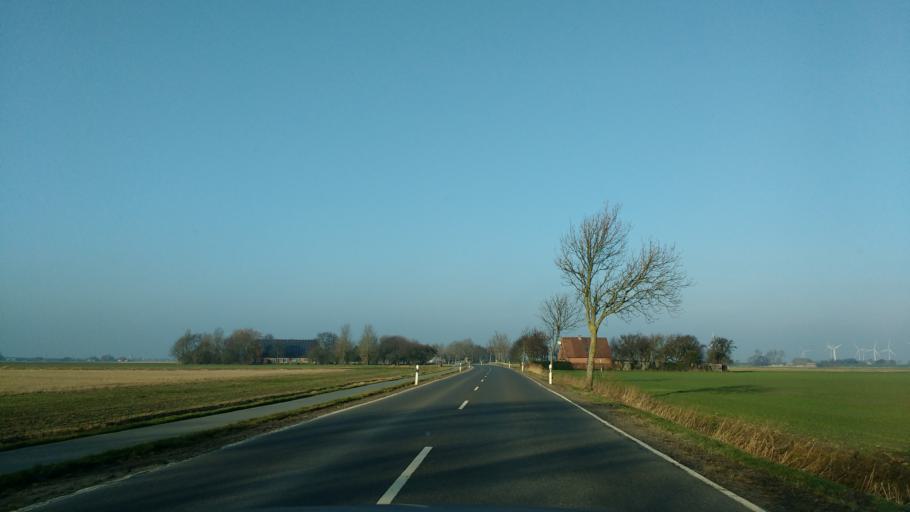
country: DE
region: Schleswig-Holstein
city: Friedrichskoog
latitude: 53.9841
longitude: 8.9145
